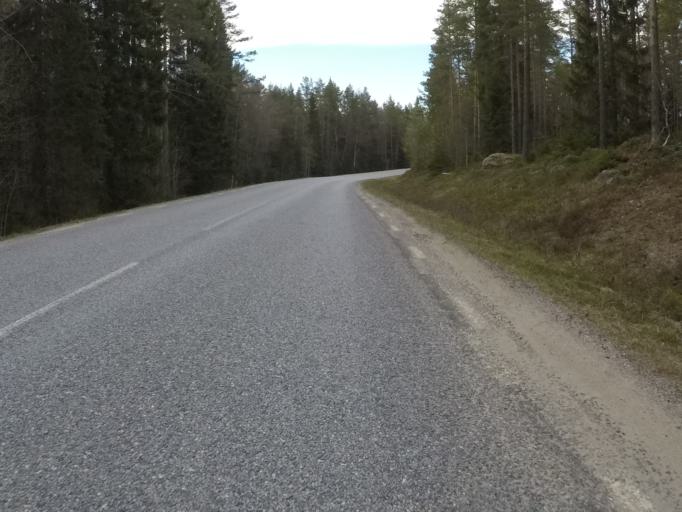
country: SE
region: Vaesterbotten
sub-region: Robertsfors Kommun
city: Robertsfors
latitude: 63.9794
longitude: 20.8104
